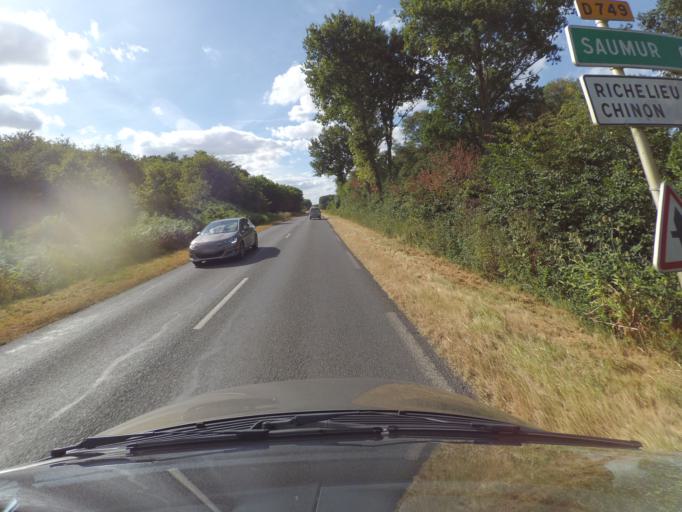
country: FR
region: Centre
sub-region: Departement d'Indre-et-Loire
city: Richelieu
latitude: 46.9938
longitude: 0.3260
